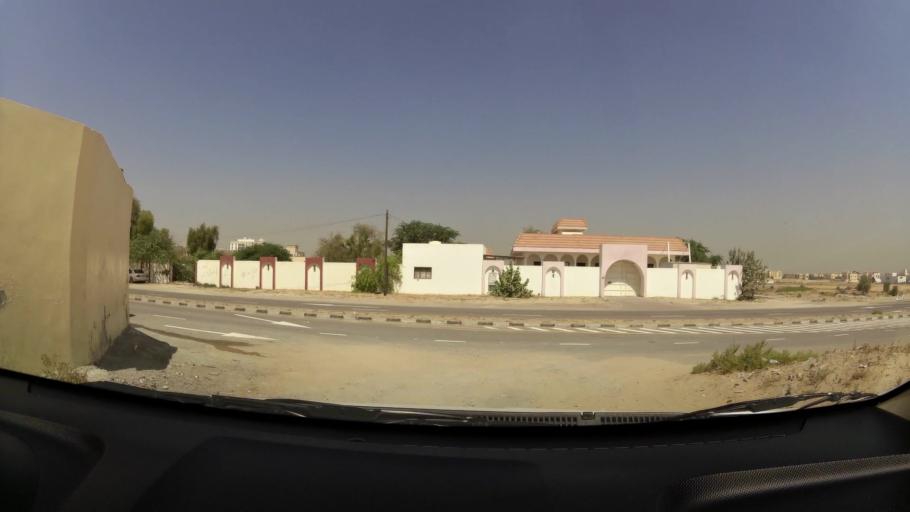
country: AE
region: Ajman
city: Ajman
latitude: 25.3974
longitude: 55.5269
